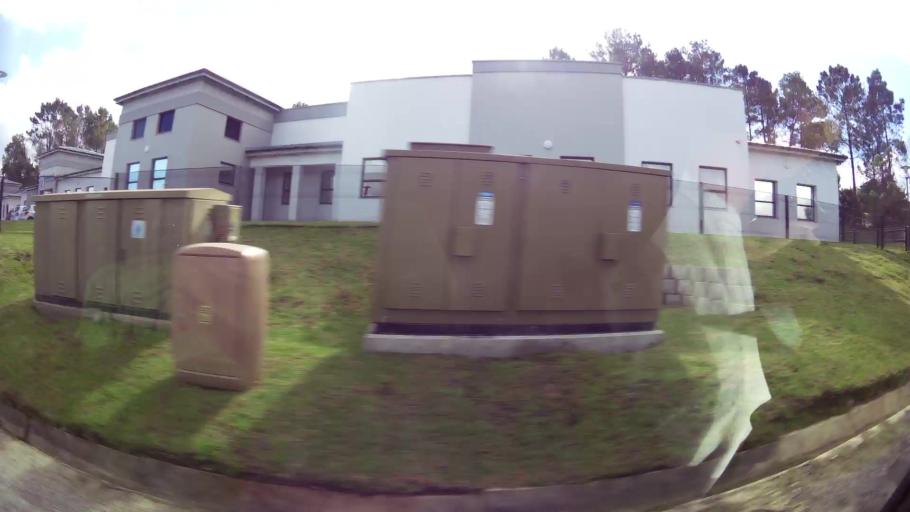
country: ZA
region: Western Cape
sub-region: Eden District Municipality
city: Knysna
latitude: -34.0522
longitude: 23.0824
